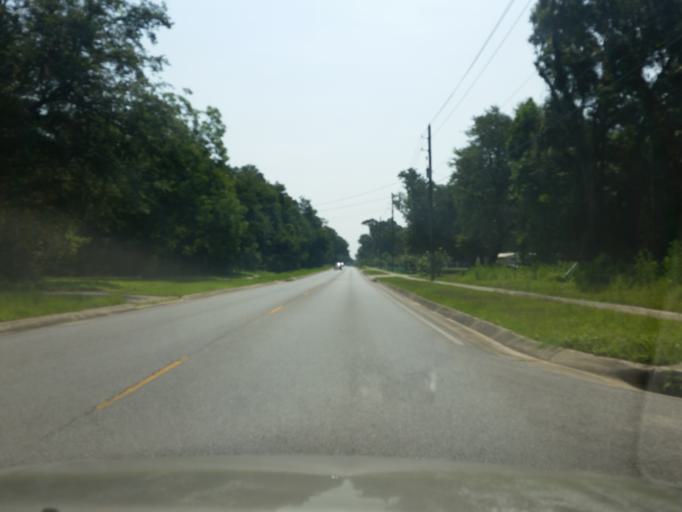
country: US
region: Florida
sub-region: Escambia County
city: Ensley
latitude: 30.5188
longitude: -87.2575
